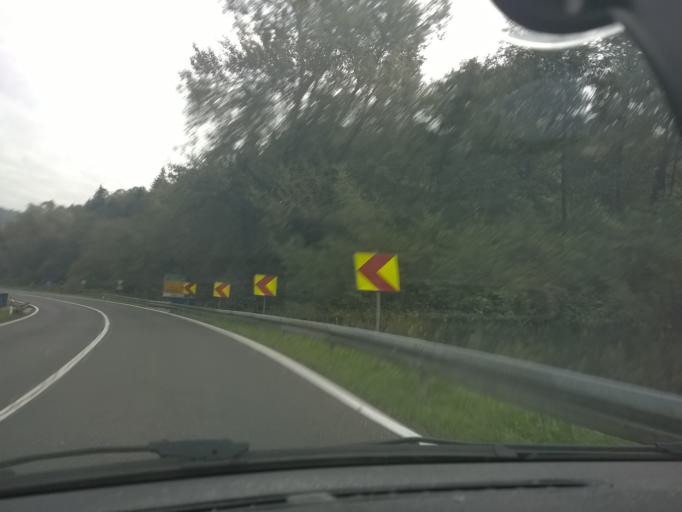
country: SI
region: Zetale
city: Zetale
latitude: 46.2613
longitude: 15.8686
